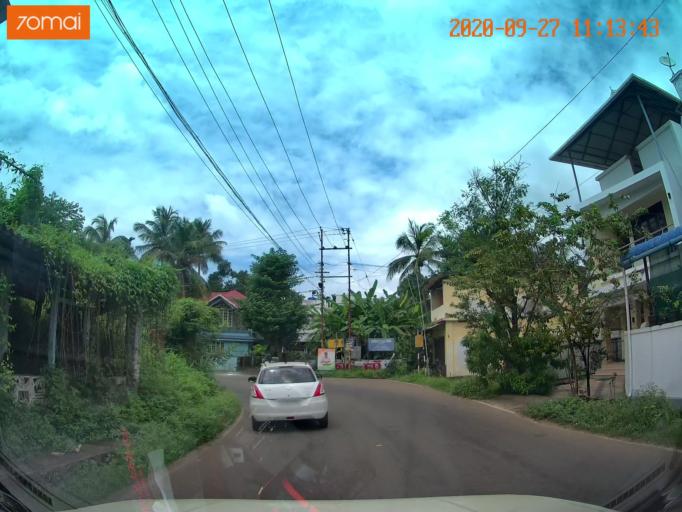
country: IN
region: Kerala
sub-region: Thrissur District
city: Thanniyam
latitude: 10.4350
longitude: 76.2075
